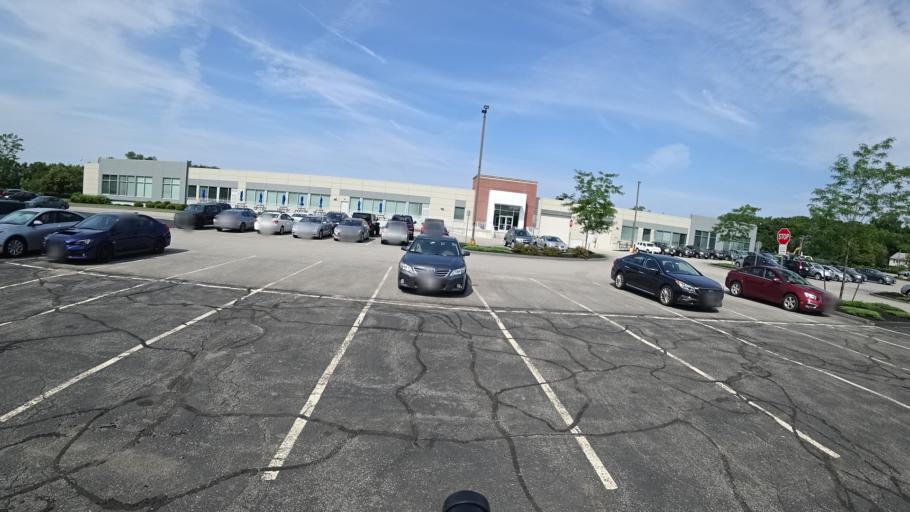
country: US
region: Massachusetts
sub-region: Norfolk County
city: Dedham
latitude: 42.2323
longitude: -71.1663
